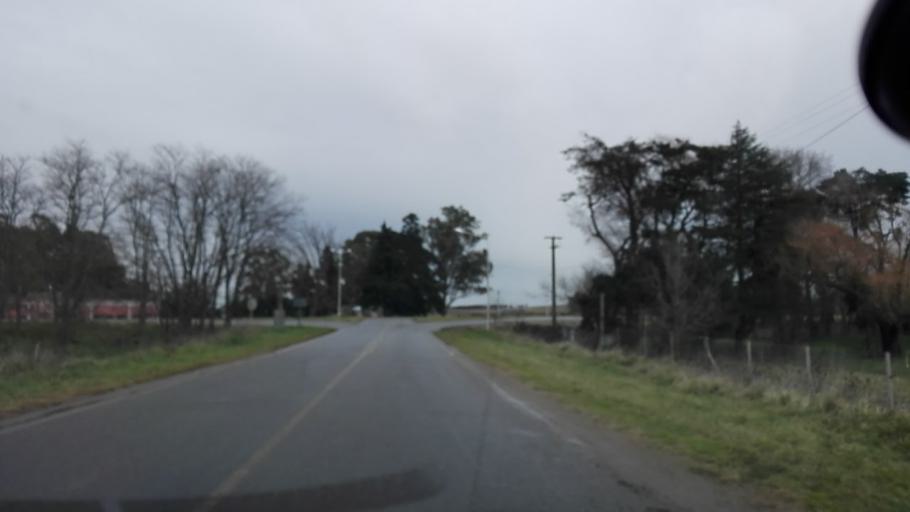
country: AR
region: Buenos Aires
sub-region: Partido de Tandil
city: Tandil
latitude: -37.3492
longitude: -59.1978
